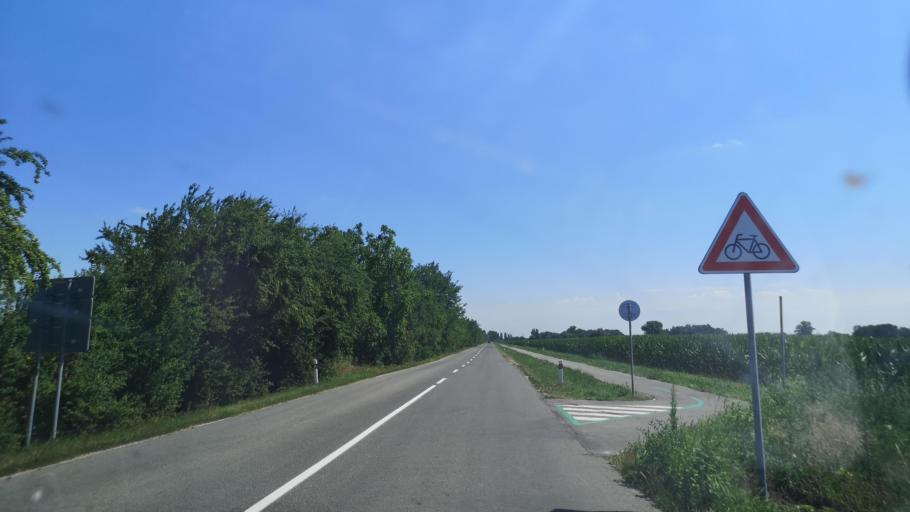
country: SK
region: Trnavsky
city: Dunajska Streda
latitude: 48.0322
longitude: 17.5446
